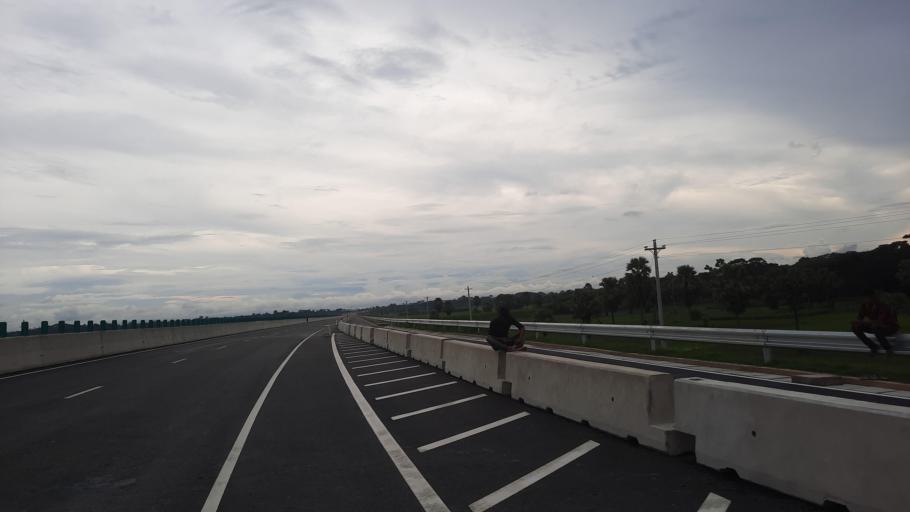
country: BD
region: Khulna
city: Kalia
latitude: 23.2063
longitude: 89.7099
